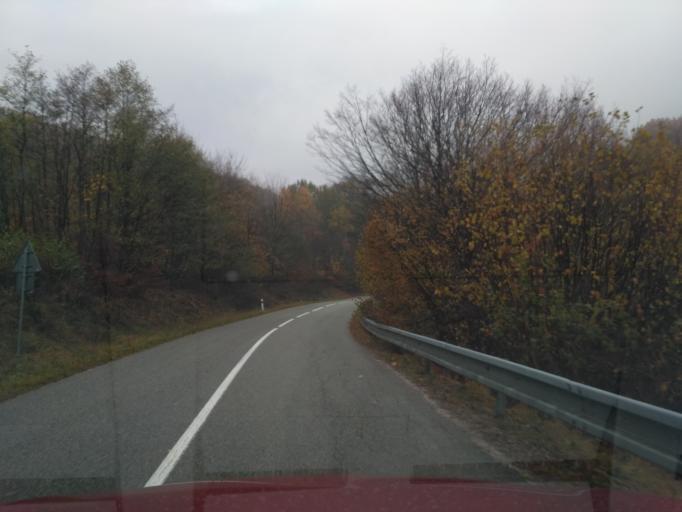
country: SK
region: Kosicky
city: Medzev
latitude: 48.7116
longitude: 20.7985
